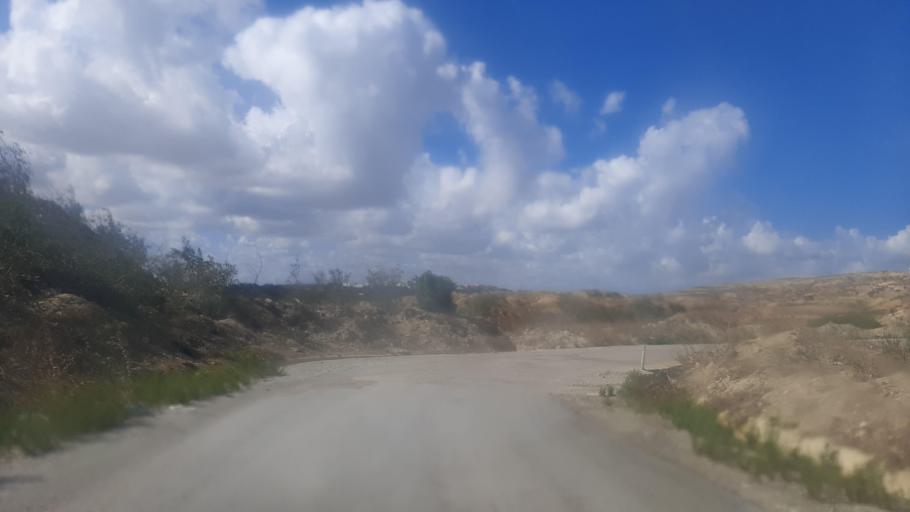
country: TN
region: Nabul
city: Nabeul
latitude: 36.4931
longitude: 10.7049
